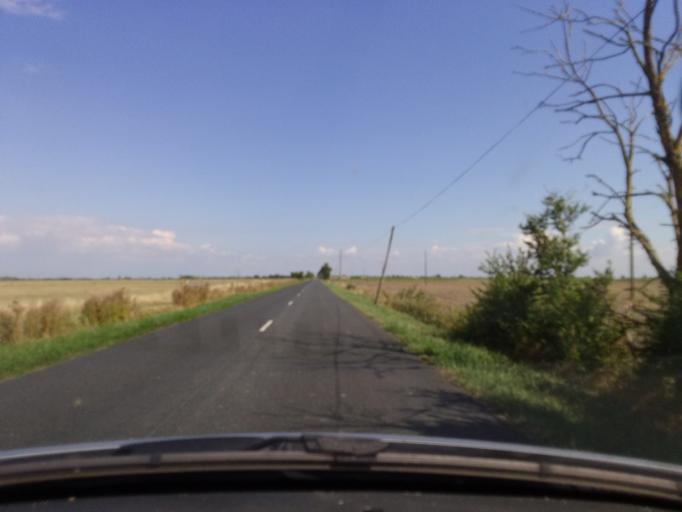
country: FR
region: Pays de la Loire
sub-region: Departement de la Vendee
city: Triaize
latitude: 46.3987
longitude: -1.2283
